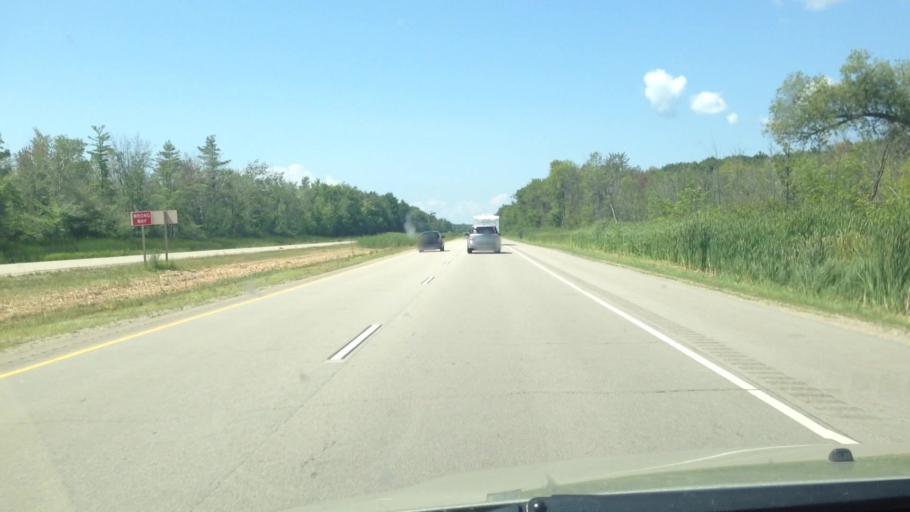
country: US
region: Wisconsin
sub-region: Oconto County
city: Oconto
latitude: 44.8120
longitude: -87.9568
